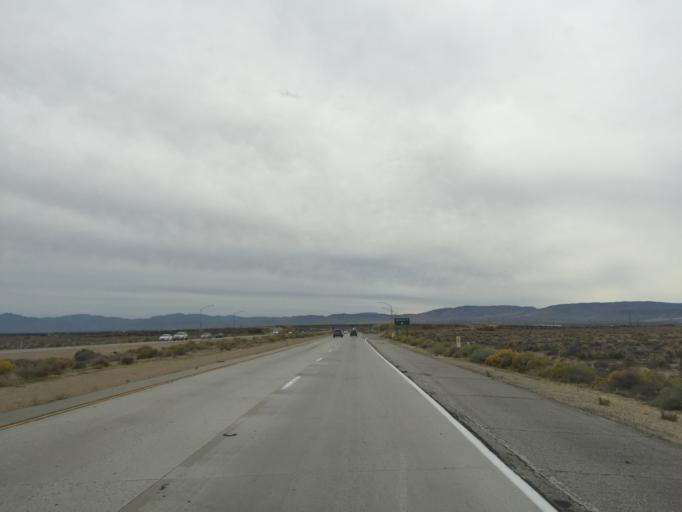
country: US
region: California
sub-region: Los Angeles County
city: Lancaster
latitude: 34.7532
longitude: -118.1707
